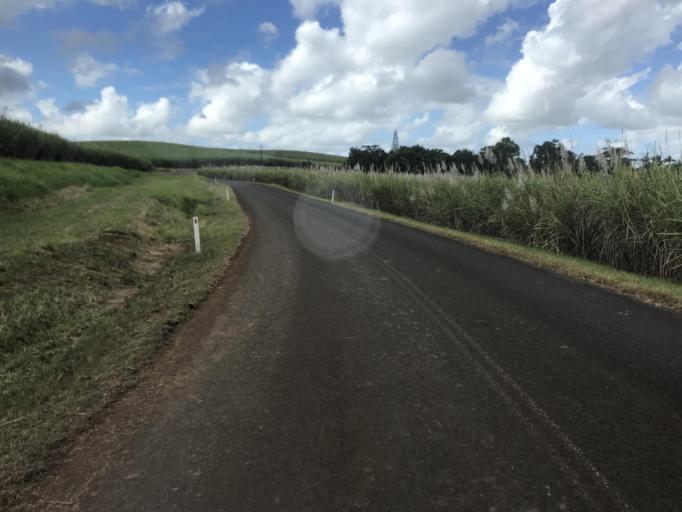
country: AU
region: Queensland
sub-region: Cassowary Coast
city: Innisfail
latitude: -17.5495
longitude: 145.8726
